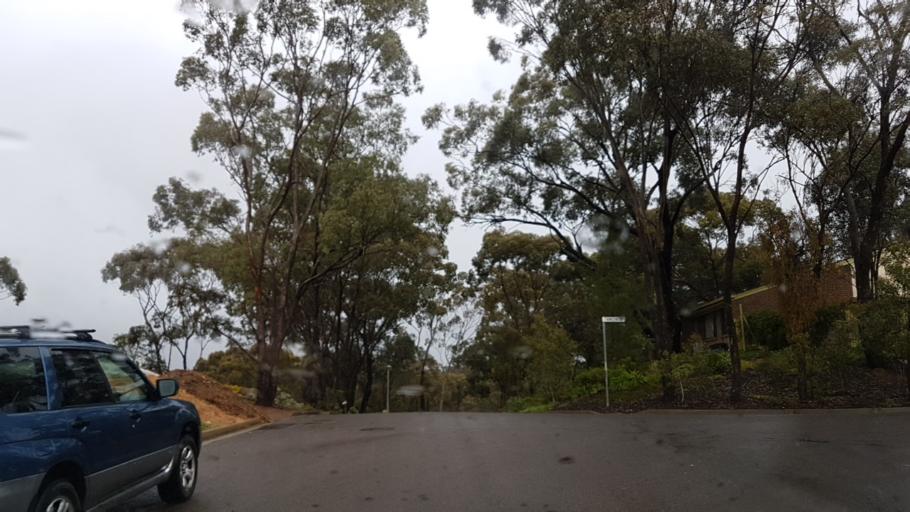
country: AU
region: South Australia
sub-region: Onkaparinga
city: Bedford Park
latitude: -35.0429
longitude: 138.5873
